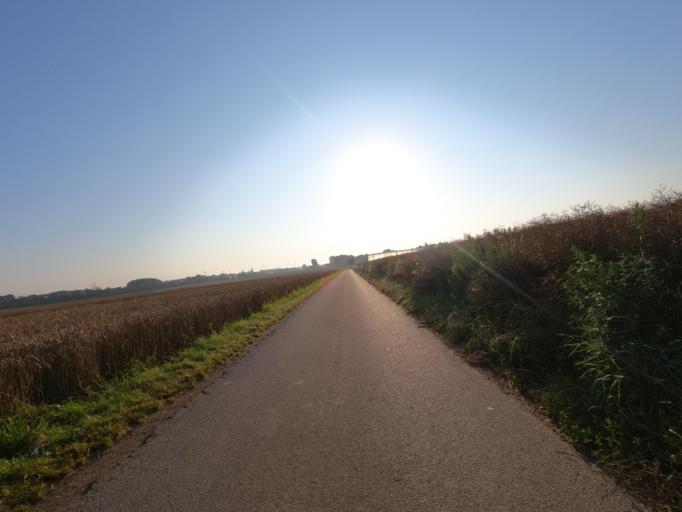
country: DE
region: North Rhine-Westphalia
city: Erkelenz
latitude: 51.0251
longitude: 6.3349
